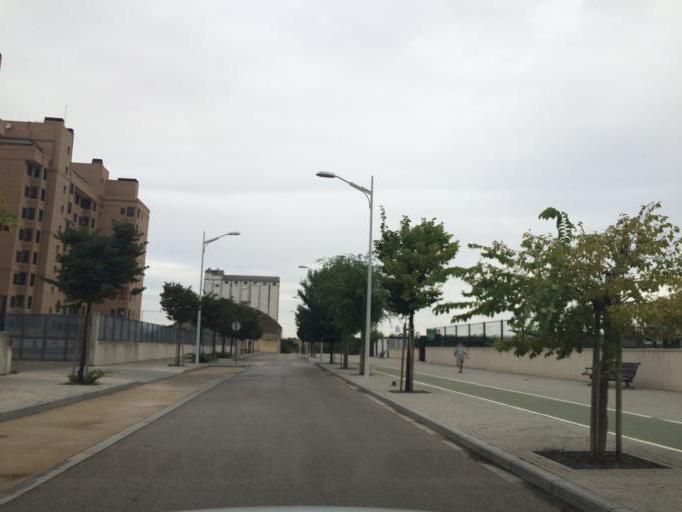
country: ES
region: Castille-La Mancha
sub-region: Provincia de Albacete
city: Albacete
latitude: 39.0091
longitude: -1.8584
